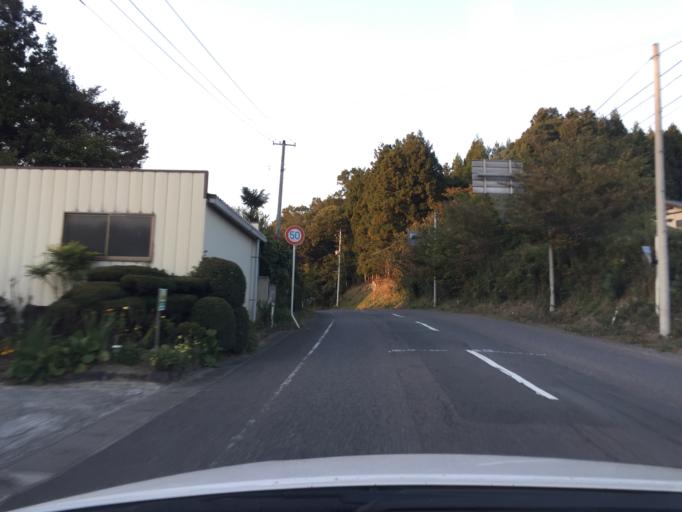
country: JP
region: Fukushima
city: Sukagawa
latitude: 37.3288
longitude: 140.4406
